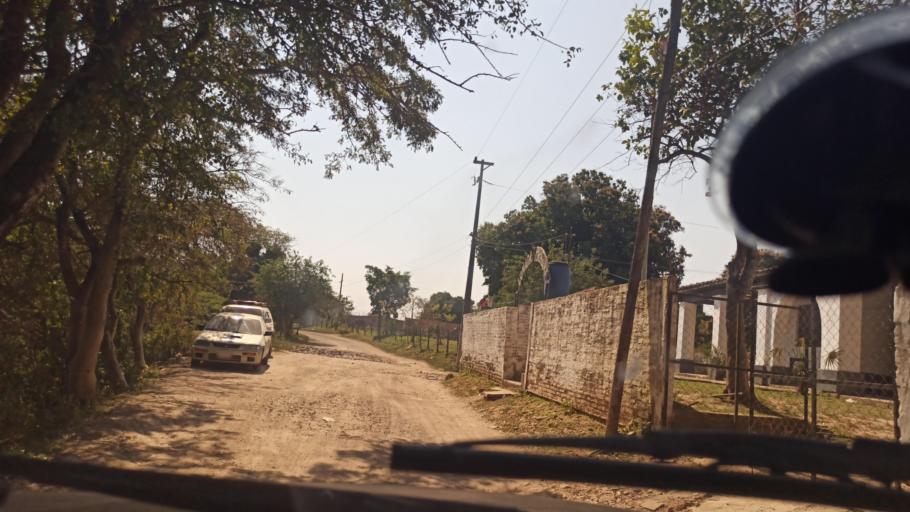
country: AR
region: Formosa
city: Clorinda
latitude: -25.3046
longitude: -57.6990
